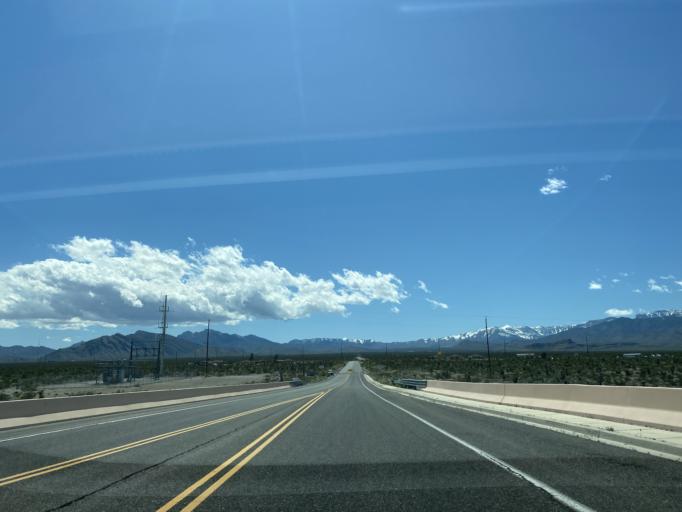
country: US
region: Nevada
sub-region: Clark County
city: Summerlin South
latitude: 36.3605
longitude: -115.3534
